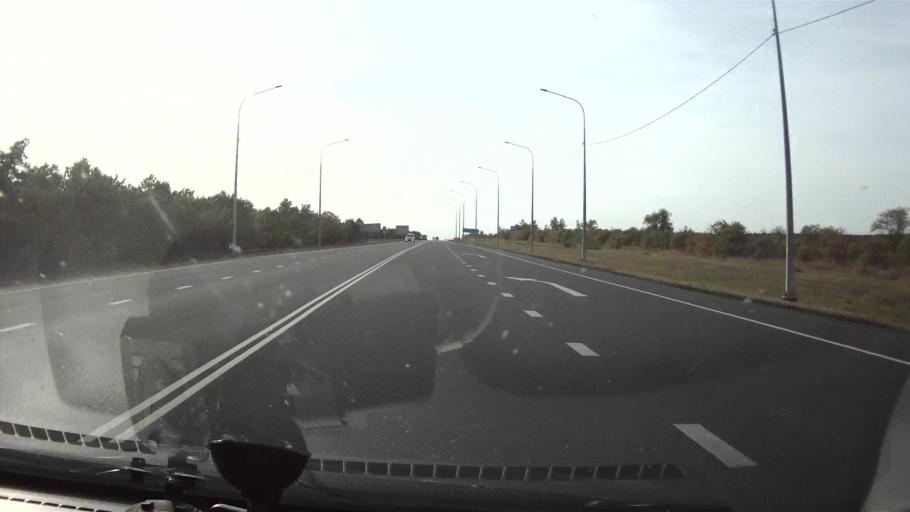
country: RU
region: Saratov
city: Yelshanka
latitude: 51.8202
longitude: 46.3530
